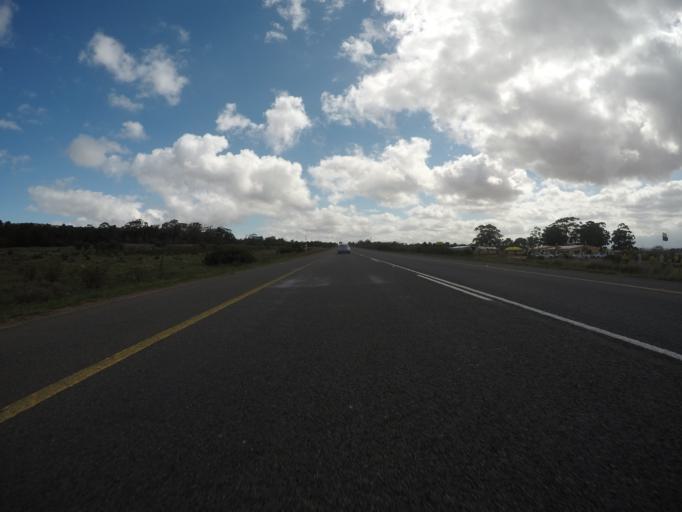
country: ZA
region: Western Cape
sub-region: Eden District Municipality
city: Riversdale
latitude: -34.2121
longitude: 21.5997
